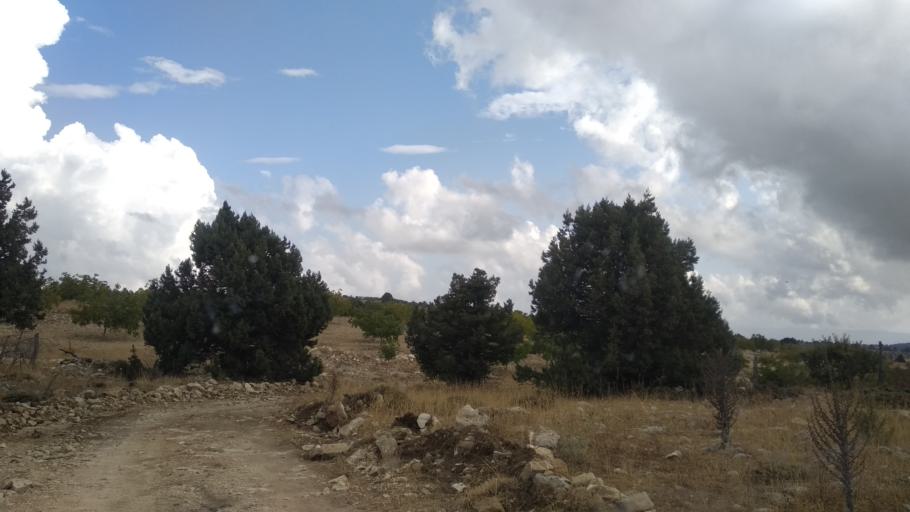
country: TR
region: Mersin
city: Sarikavak
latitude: 36.5709
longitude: 33.7550
